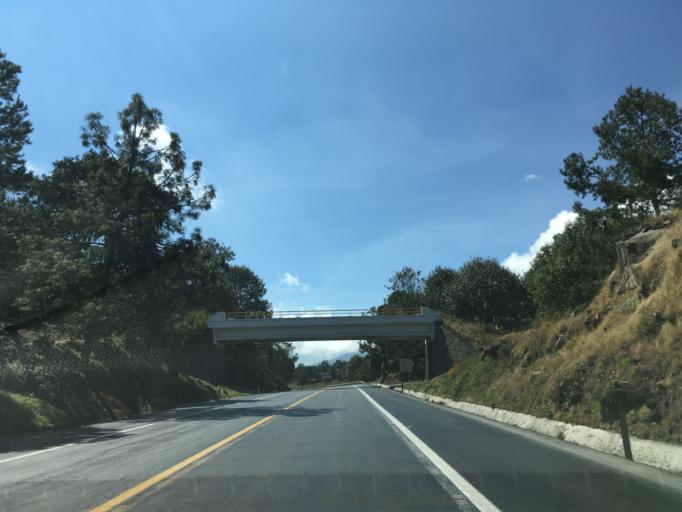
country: MX
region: Michoacan
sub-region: Patzcuaro
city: Santa Maria Huiramangaro (San Juan Tumbio)
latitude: 19.4874
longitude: -101.7198
